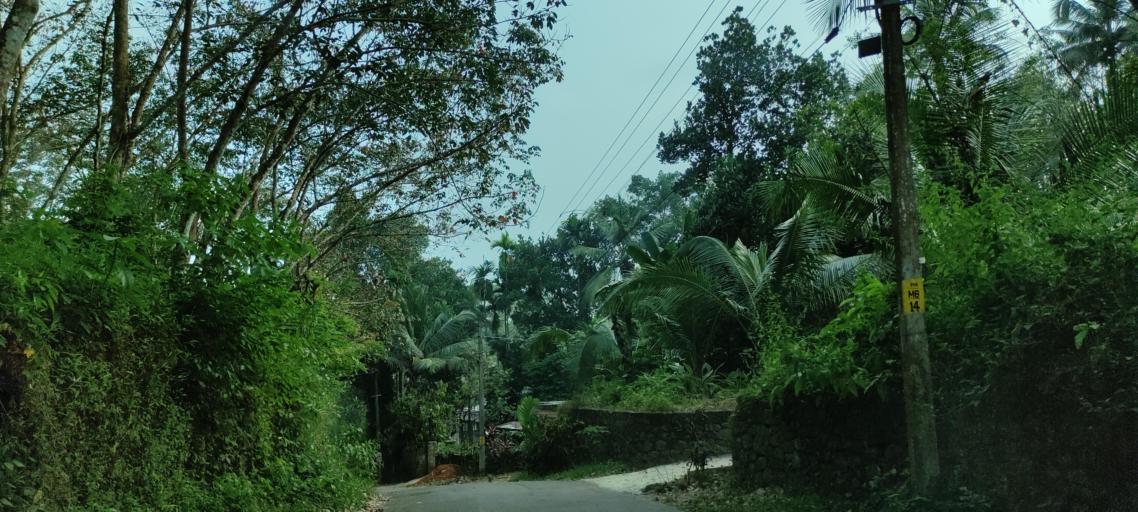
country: IN
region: Kerala
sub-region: Ernakulam
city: Piravam
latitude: 9.8076
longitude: 76.5351
